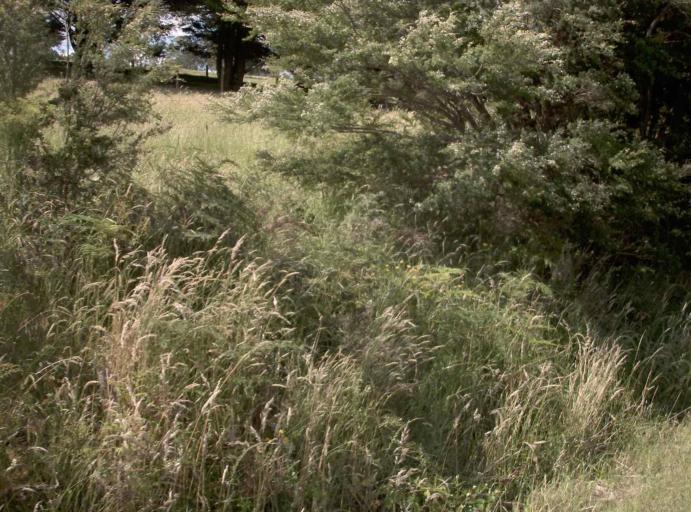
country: AU
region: Victoria
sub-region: Latrobe
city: Morwell
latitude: -38.1498
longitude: 146.4399
